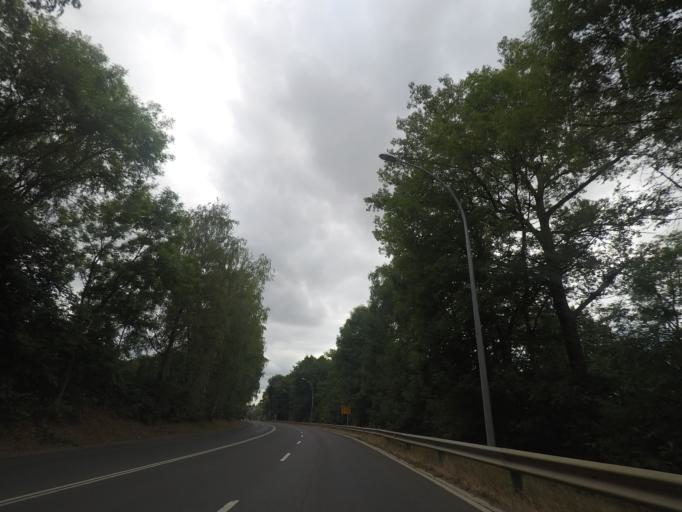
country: LU
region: Luxembourg
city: Kirchberg
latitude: 49.6153
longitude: 6.1702
